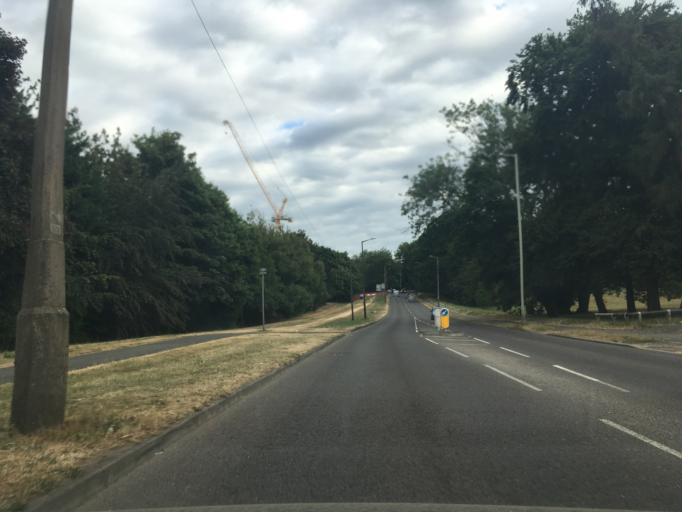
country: GB
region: England
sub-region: Hertfordshire
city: Hemel Hempstead
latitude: 51.7687
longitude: -0.4487
